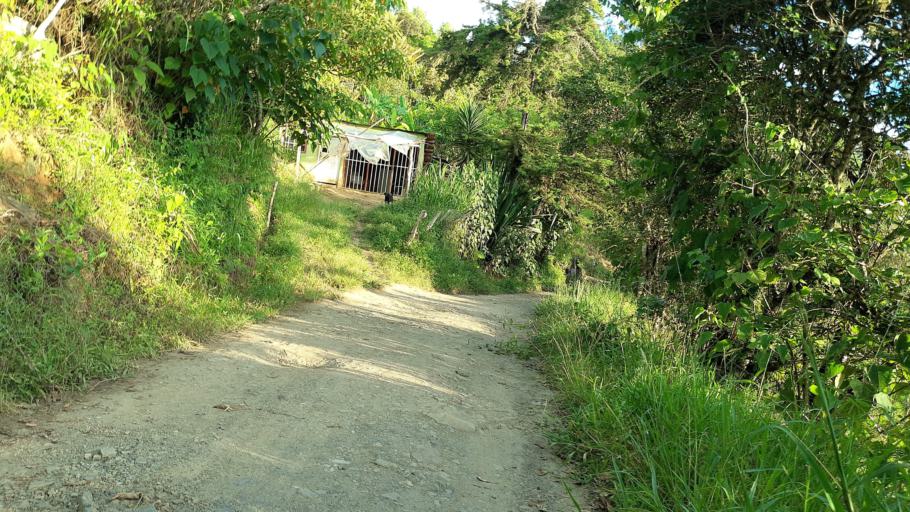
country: CO
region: Boyaca
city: Garagoa
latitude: 5.0653
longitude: -73.3763
